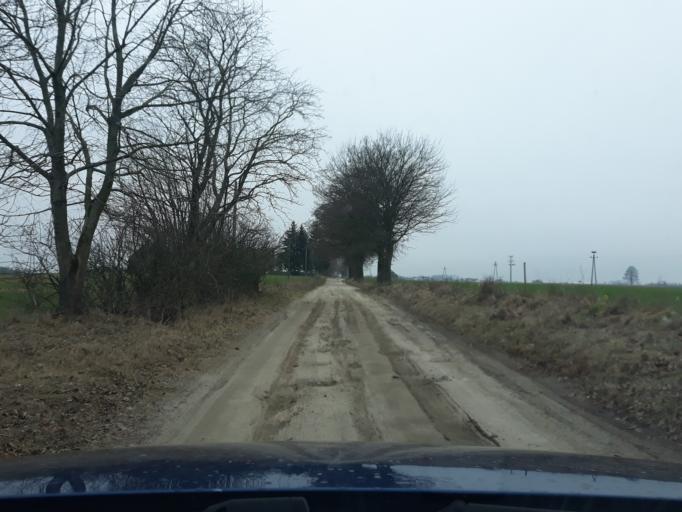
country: PL
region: Pomeranian Voivodeship
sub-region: Powiat czluchowski
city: Czluchow
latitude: 53.8182
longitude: 17.4170
